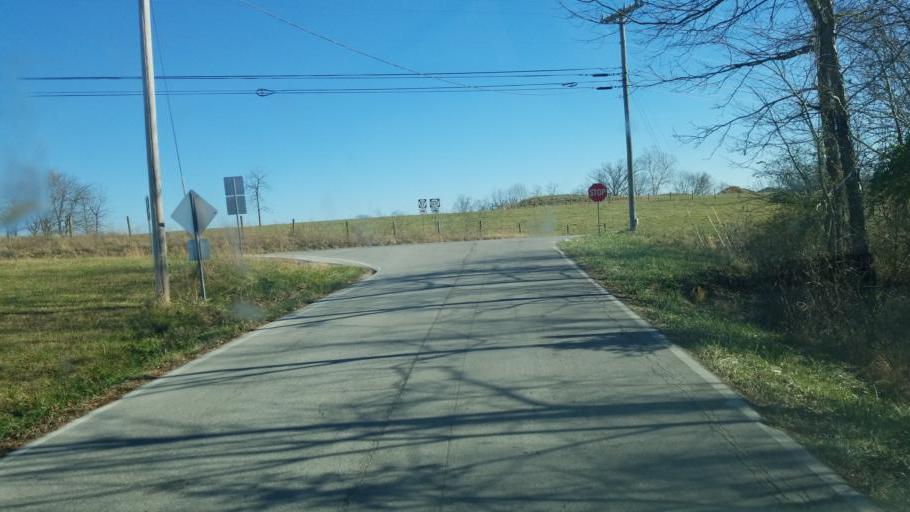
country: US
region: Ohio
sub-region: Adams County
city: Manchester
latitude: 38.5322
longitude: -83.6205
